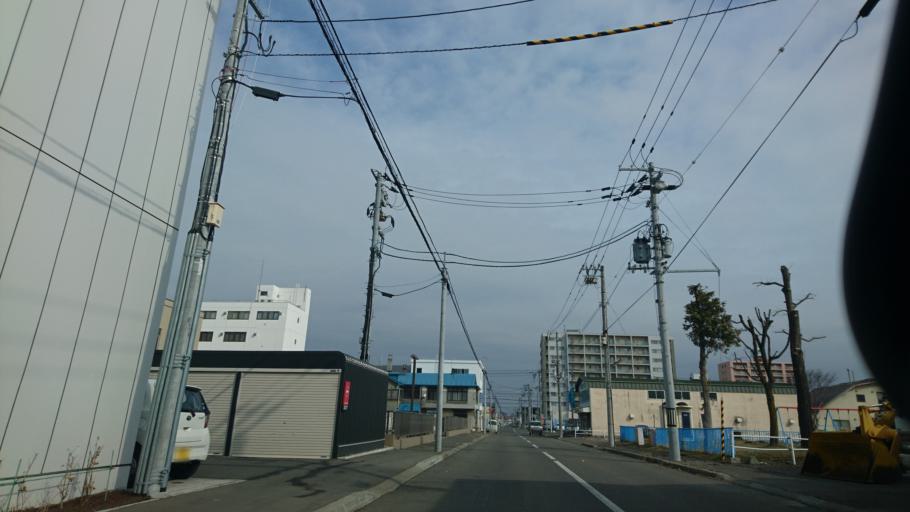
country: JP
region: Hokkaido
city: Obihiro
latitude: 42.9230
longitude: 143.2061
